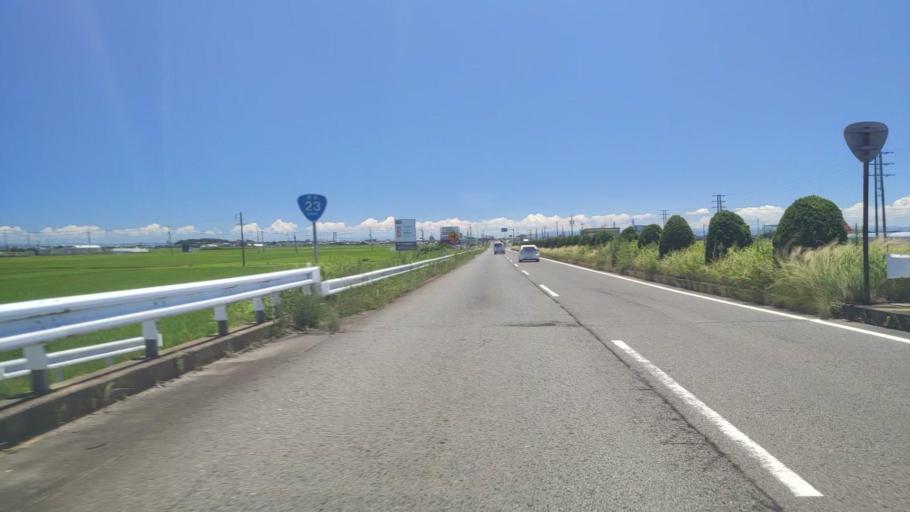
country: JP
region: Mie
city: Suzuka
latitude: 34.8873
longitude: 136.5992
